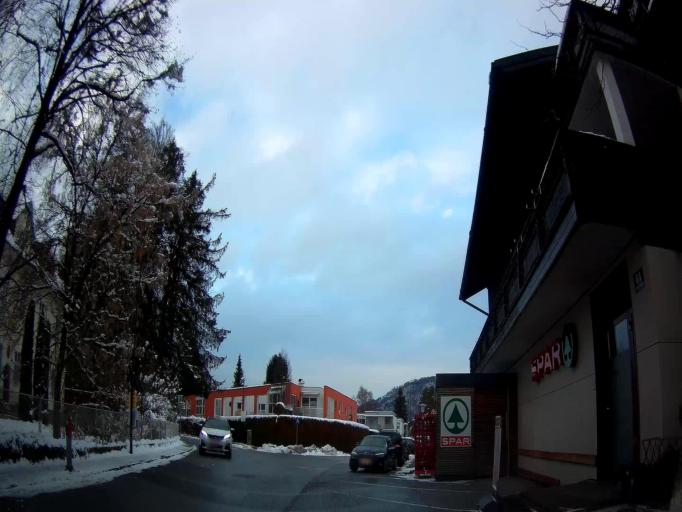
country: AT
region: Salzburg
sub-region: Politischer Bezirk Salzburg-Umgebung
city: Elsbethen
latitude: 47.7882
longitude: 13.0830
